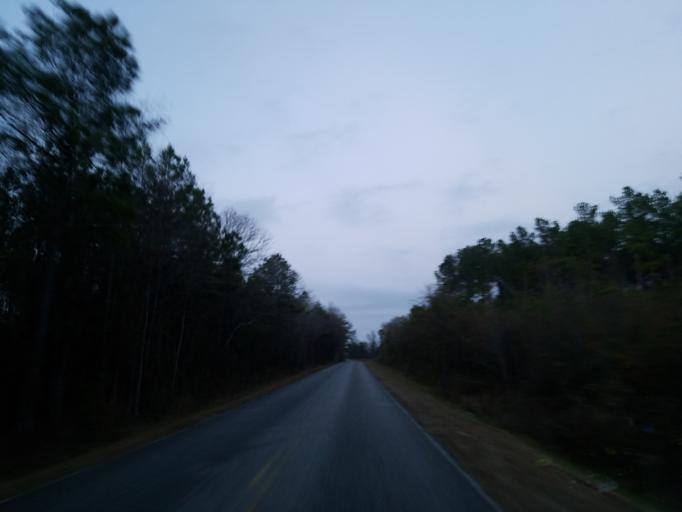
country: US
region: Alabama
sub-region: Sumter County
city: York
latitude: 32.4090
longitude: -88.4411
